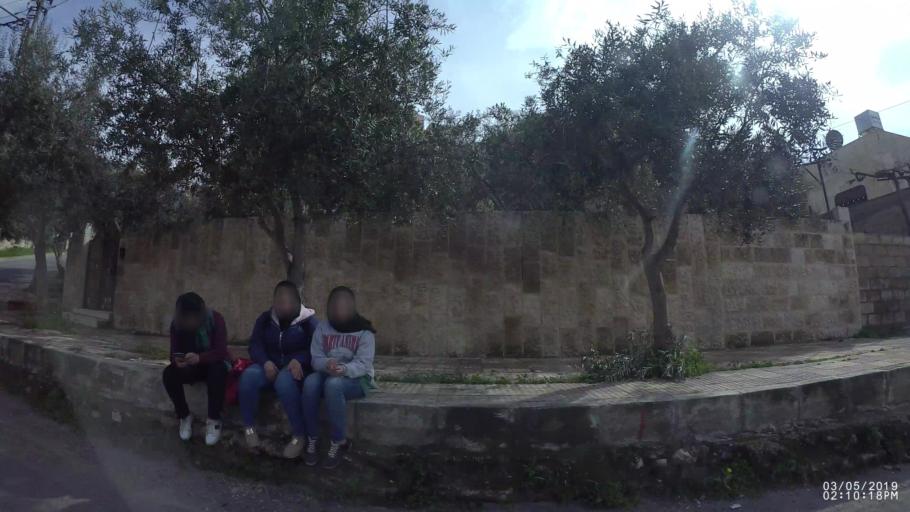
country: JO
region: Amman
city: Amman
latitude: 32.0060
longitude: 35.9407
